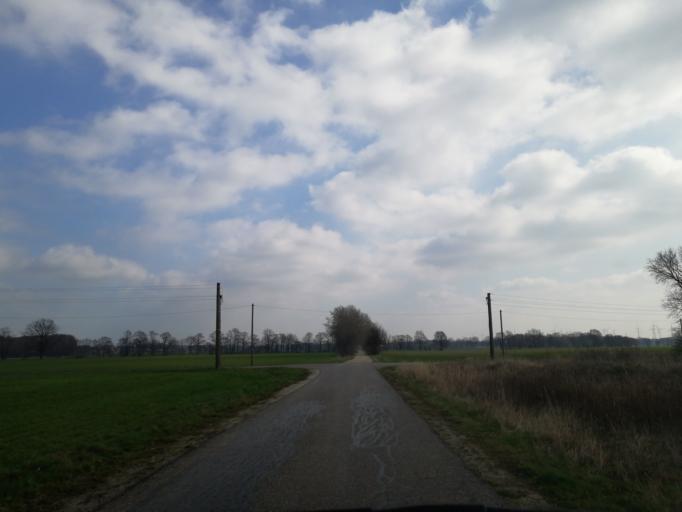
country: DE
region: Brandenburg
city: Finsterwalde
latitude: 51.6586
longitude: 13.7173
